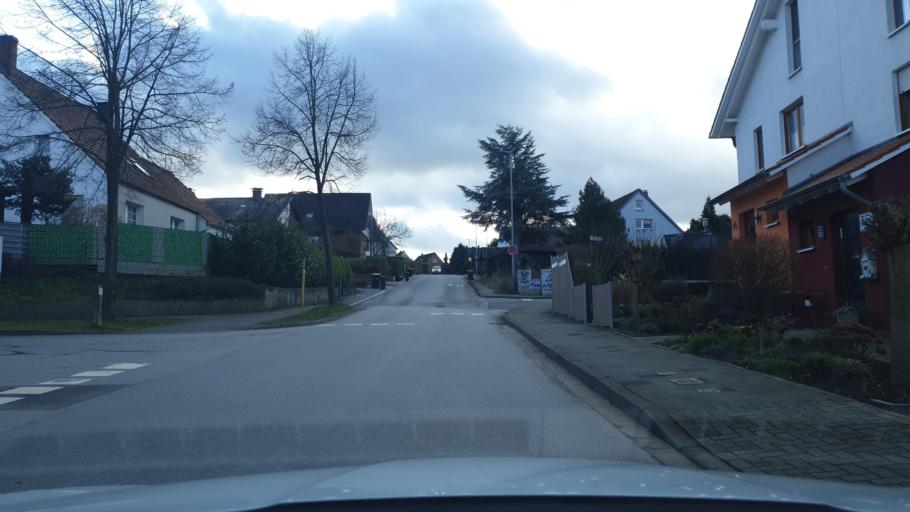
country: DE
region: North Rhine-Westphalia
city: Bad Oeynhausen
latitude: 52.1936
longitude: 8.8347
